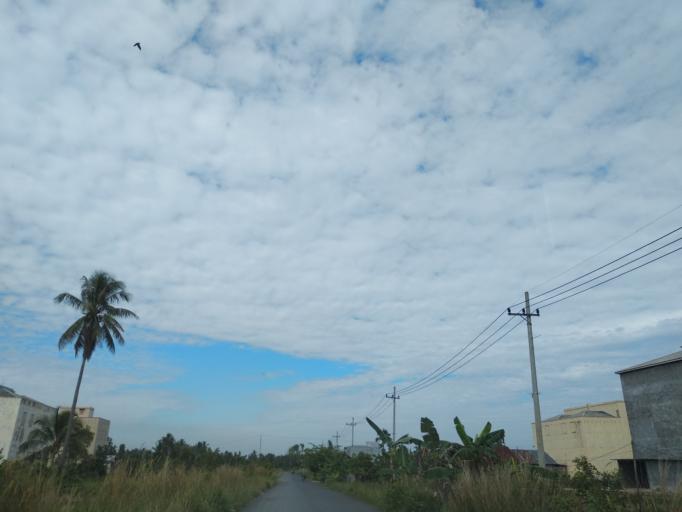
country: ID
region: South Kalimantan
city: Anjirmuara
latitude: -3.2044
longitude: 114.5421
